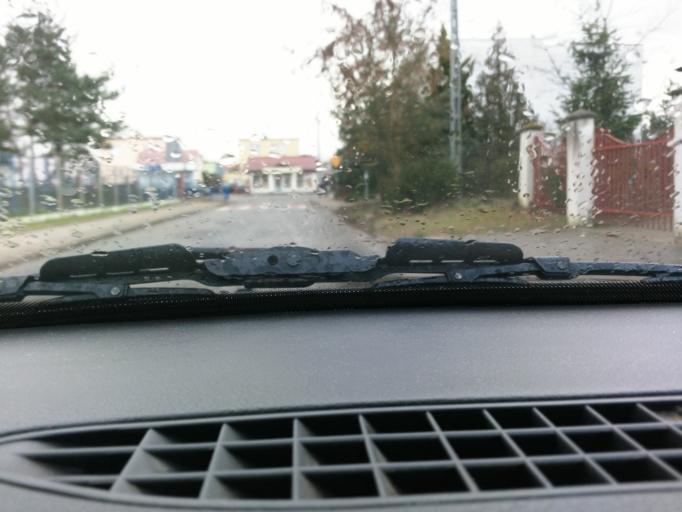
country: PL
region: Kujawsko-Pomorskie
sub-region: Grudziadz
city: Grudziadz
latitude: 53.4281
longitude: 18.7267
